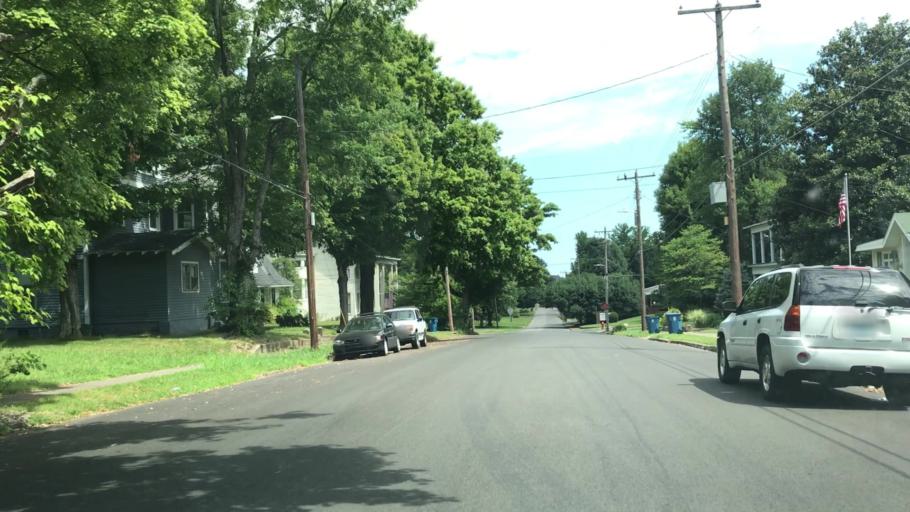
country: US
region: Kentucky
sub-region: Graves County
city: Mayfield
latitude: 36.7444
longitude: -88.6333
